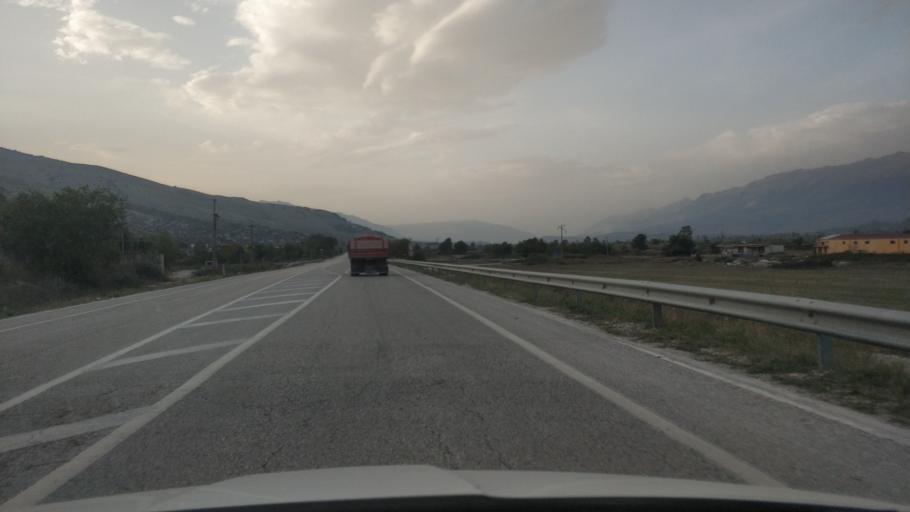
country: AL
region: Gjirokaster
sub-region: Rrethi i Gjirokastres
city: Libohove
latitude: 39.9505
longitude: 20.2561
